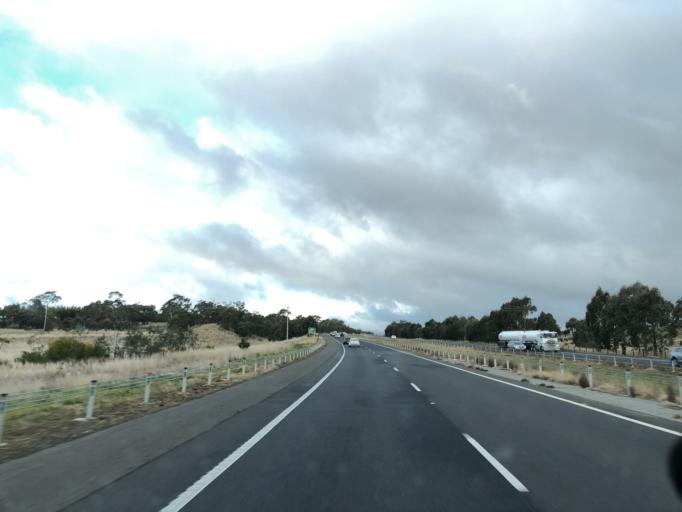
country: AU
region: Victoria
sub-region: Mount Alexander
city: Castlemaine
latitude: -37.2715
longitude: 144.4794
